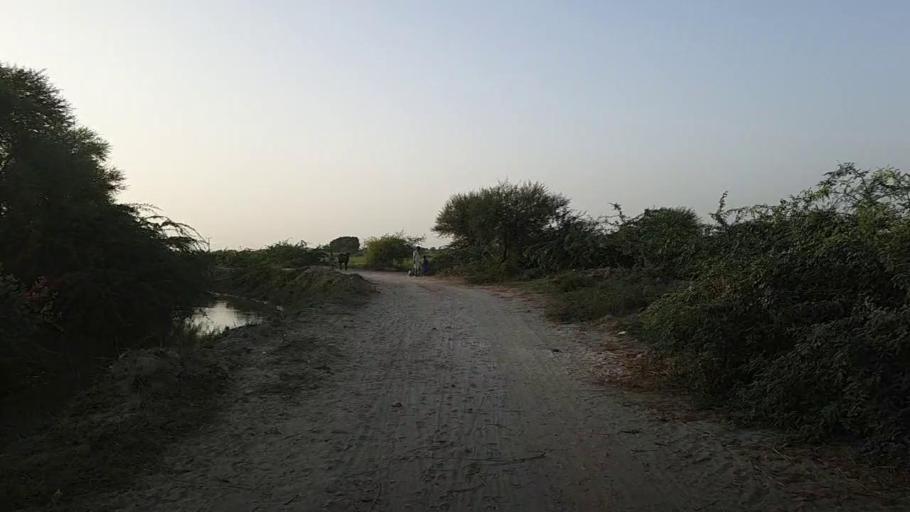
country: PK
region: Sindh
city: Kario
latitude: 24.7078
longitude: 68.4648
